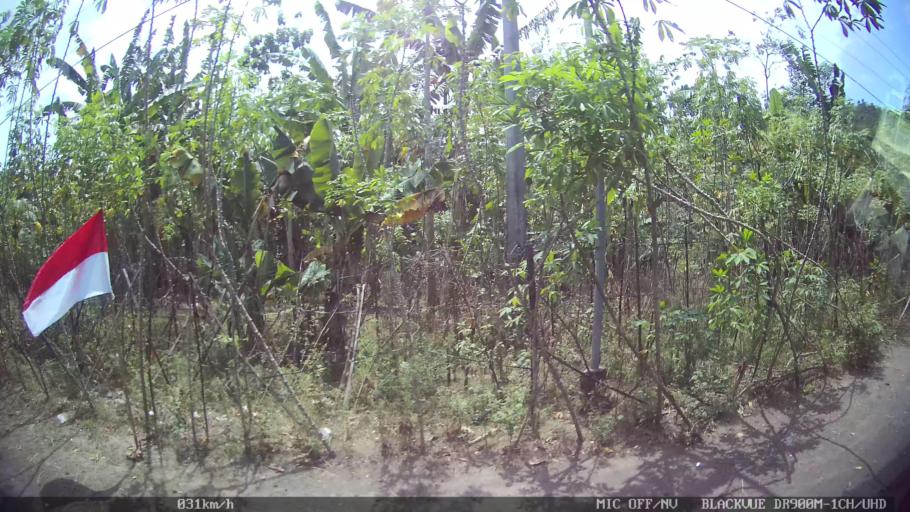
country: ID
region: Central Java
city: Candi Prambanan
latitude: -7.8131
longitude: 110.5120
